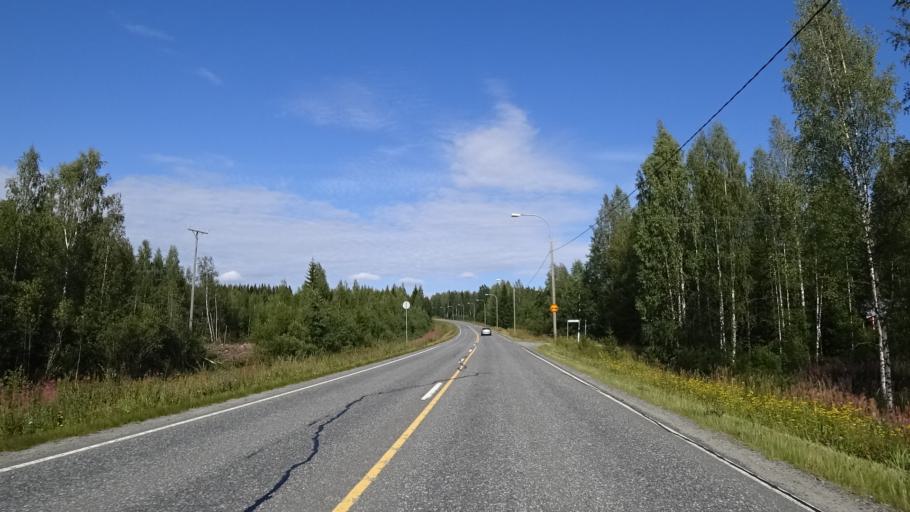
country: FI
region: North Karelia
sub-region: Joensuu
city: Eno
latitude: 62.7788
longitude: 30.0678
